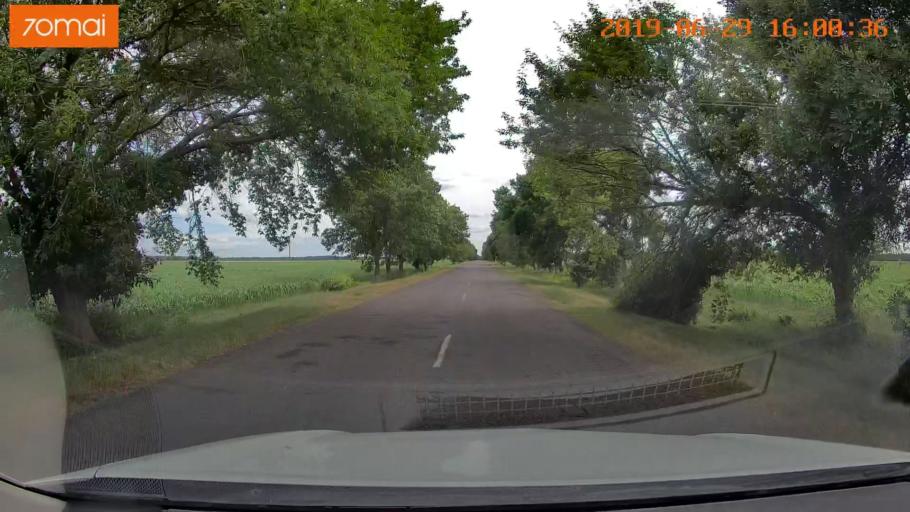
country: BY
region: Brest
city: Luninyets
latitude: 52.2583
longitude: 27.0173
